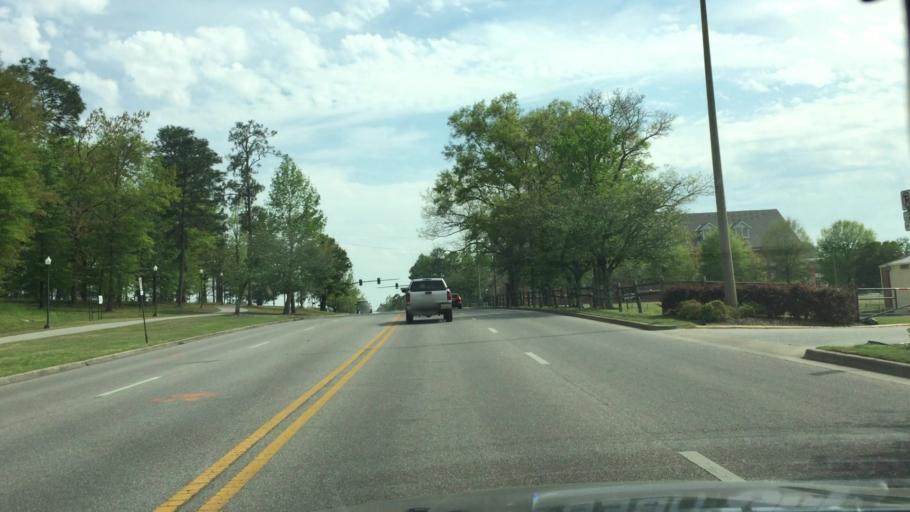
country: US
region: Alabama
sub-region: Lee County
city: Auburn
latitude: 32.5941
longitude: -85.4903
